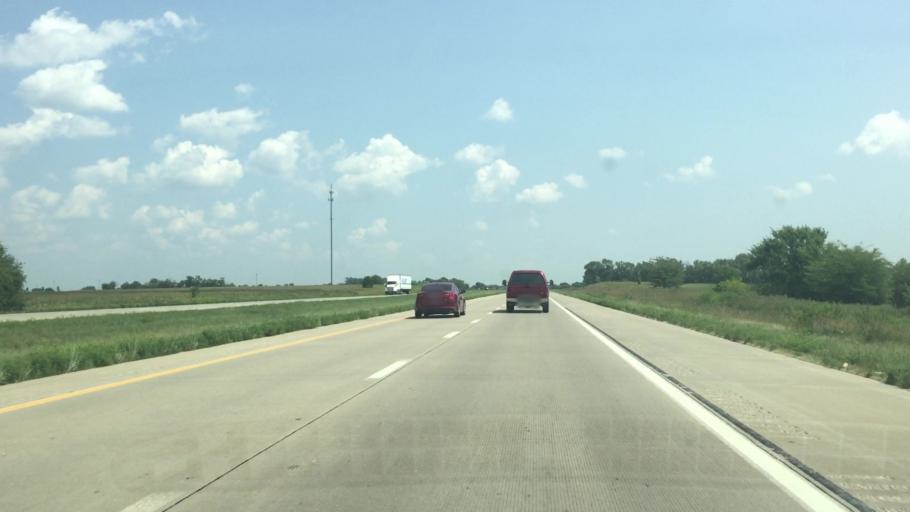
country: US
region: Kansas
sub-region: Franklin County
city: Wellsville
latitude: 38.6873
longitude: -95.1169
